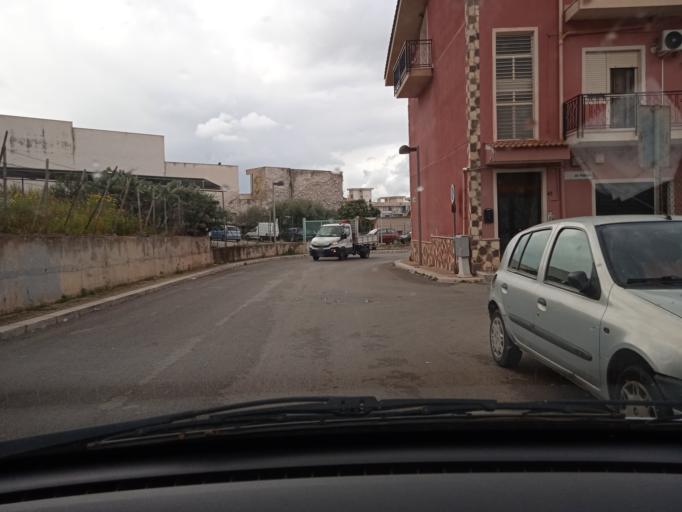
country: IT
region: Sicily
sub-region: Palermo
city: Villabate
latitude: 38.0741
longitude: 13.4440
